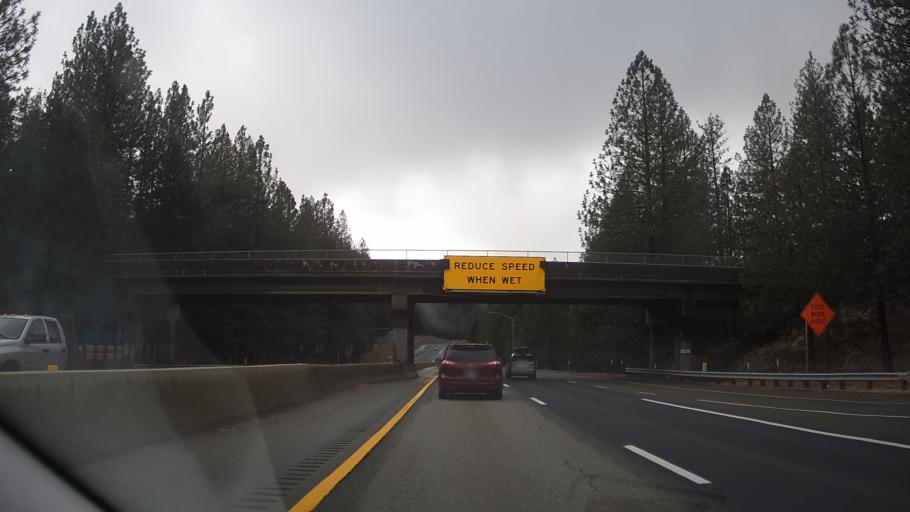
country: US
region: California
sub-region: Placer County
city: Colfax
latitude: 39.1502
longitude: -120.8978
